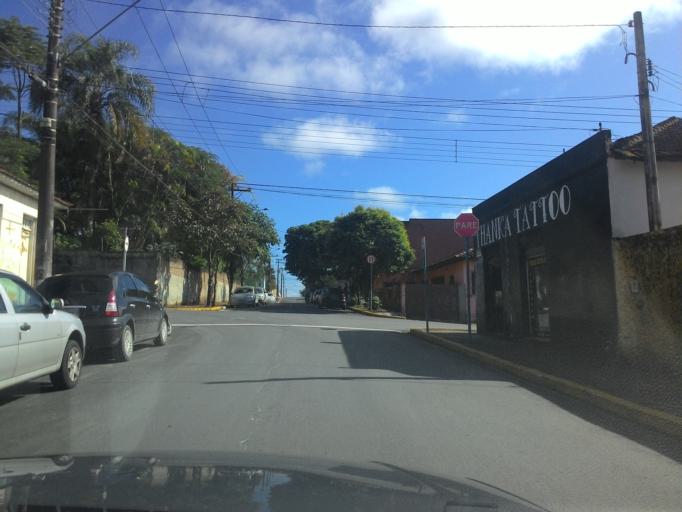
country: BR
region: Sao Paulo
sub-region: Registro
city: Registro
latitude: -24.4926
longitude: -47.8453
